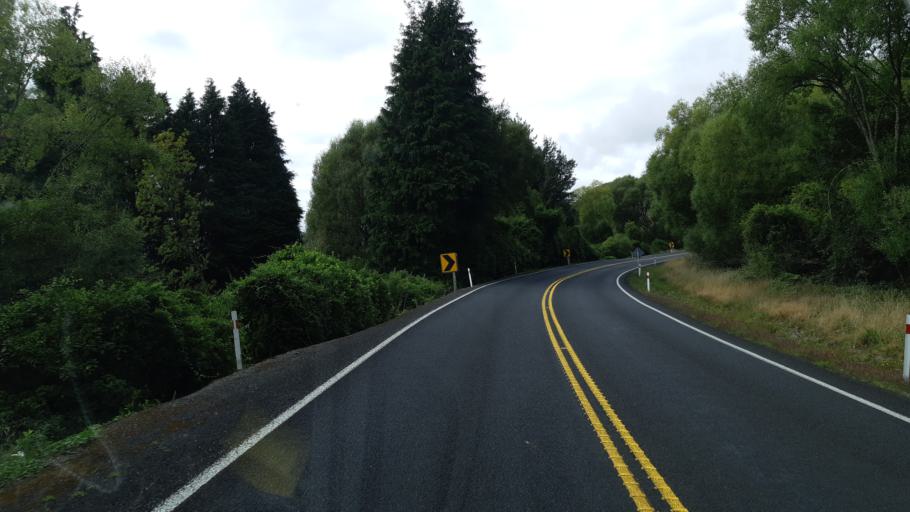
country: NZ
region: West Coast
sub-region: Buller District
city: Westport
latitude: -41.7809
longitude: 172.2732
